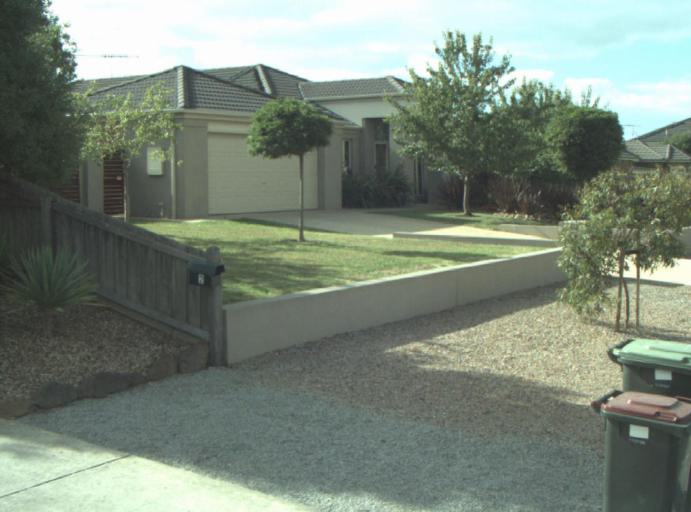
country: AU
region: Victoria
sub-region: Greater Geelong
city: Wandana Heights
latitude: -38.2124
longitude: 144.3002
